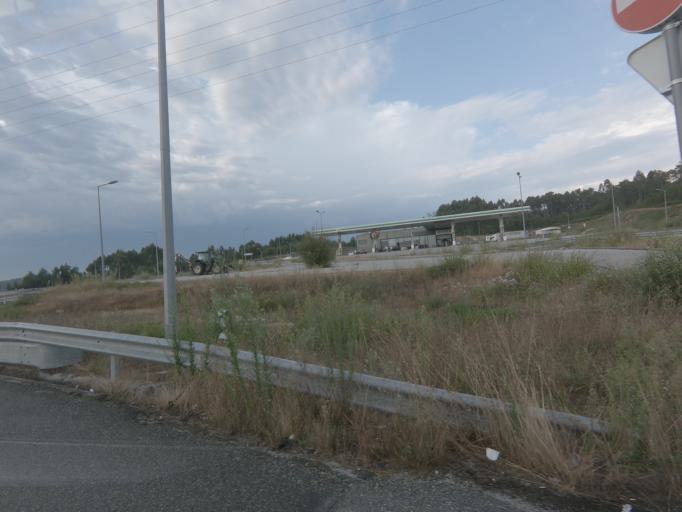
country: PT
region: Viseu
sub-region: Viseu
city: Campo
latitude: 40.7069
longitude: -7.9441
